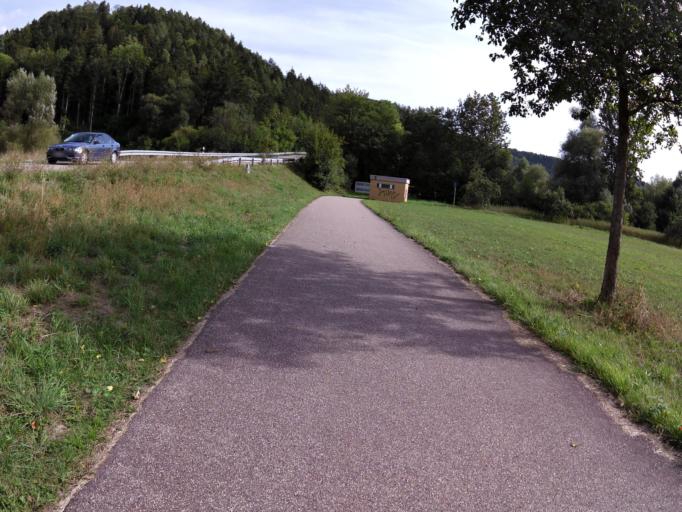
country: DE
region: Baden-Wuerttemberg
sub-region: Freiburg Region
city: Epfendorf
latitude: 48.2630
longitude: 8.6056
